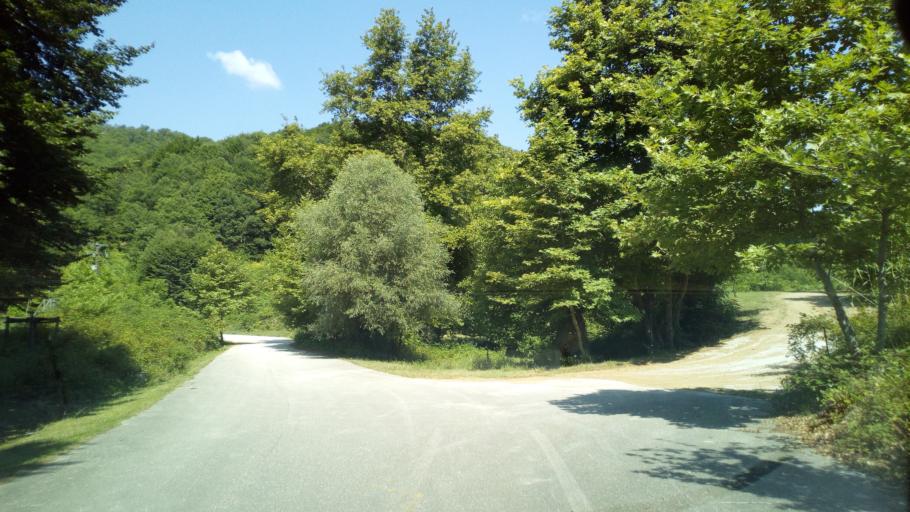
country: GR
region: Central Macedonia
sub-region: Nomos Thessalonikis
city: Sochos
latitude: 40.8291
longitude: 23.3501
